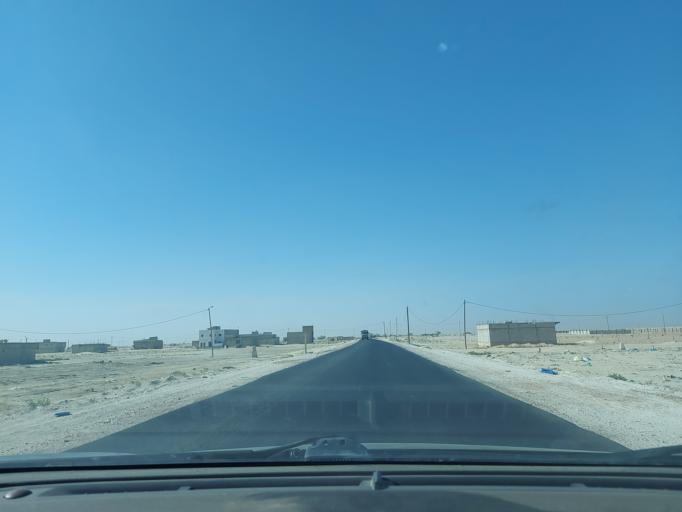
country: MR
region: Nouakchott
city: Nouakchott
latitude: 17.9966
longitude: -15.9882
